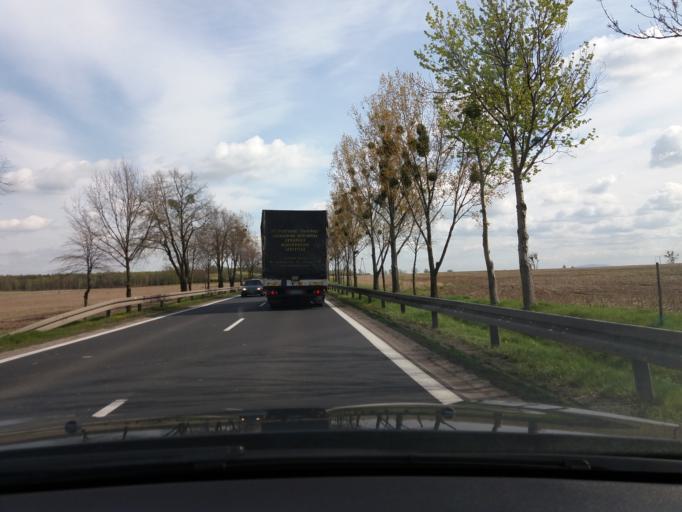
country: PL
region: Lower Silesian Voivodeship
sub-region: Powiat sredzki
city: Ciechow
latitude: 51.1751
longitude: 16.5363
